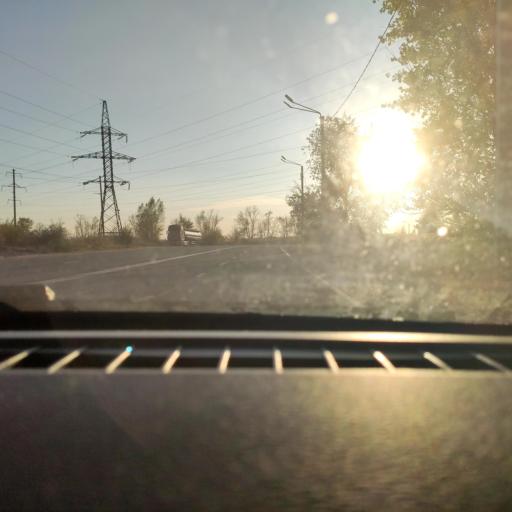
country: RU
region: Voronezj
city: Maslovka
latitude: 51.6221
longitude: 39.2745
